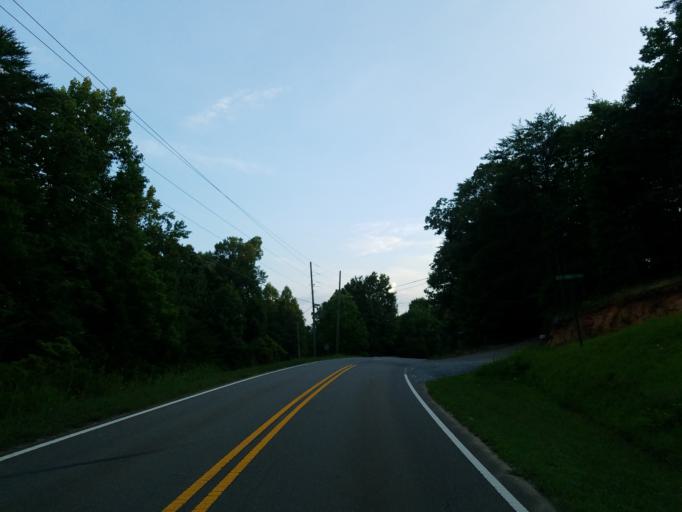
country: US
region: Georgia
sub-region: Pickens County
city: Jasper
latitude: 34.5461
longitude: -84.4712
